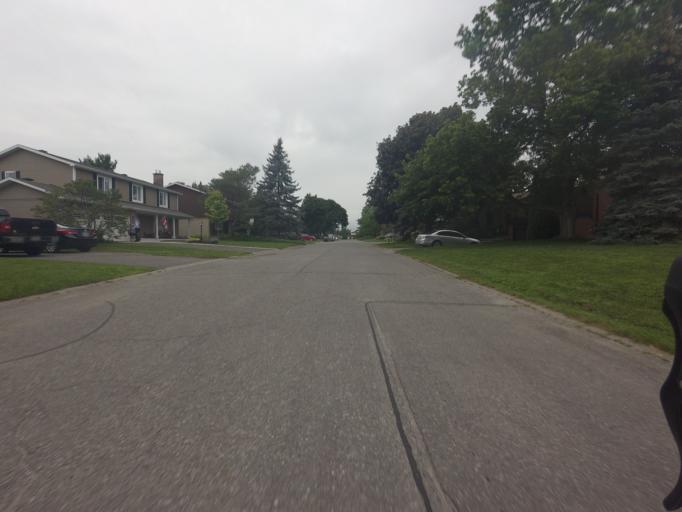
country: CA
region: Ontario
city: Ottawa
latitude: 45.3485
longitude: -75.7475
